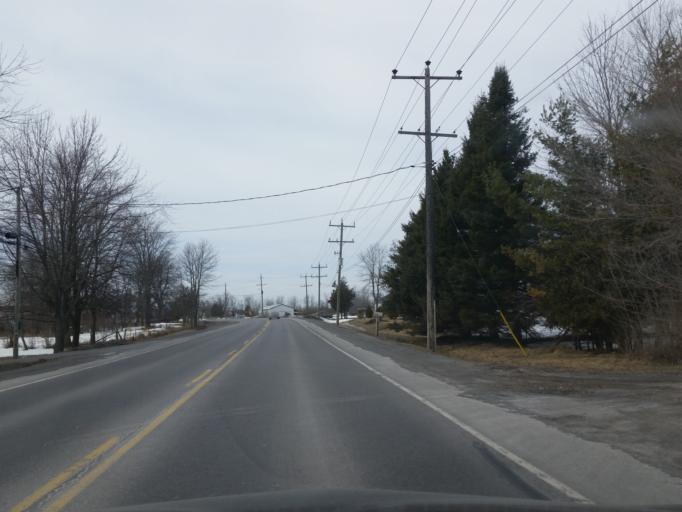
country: CA
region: Ontario
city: Skatepark
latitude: 44.2739
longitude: -76.7435
